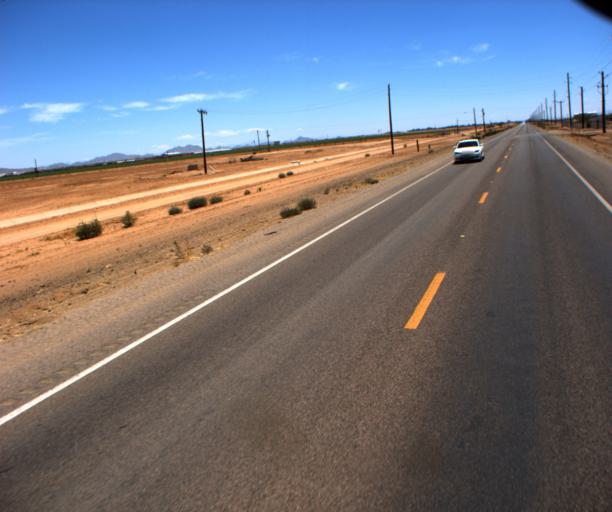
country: US
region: Arizona
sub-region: Pinal County
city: Casa Grande
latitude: 32.8794
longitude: -111.9234
